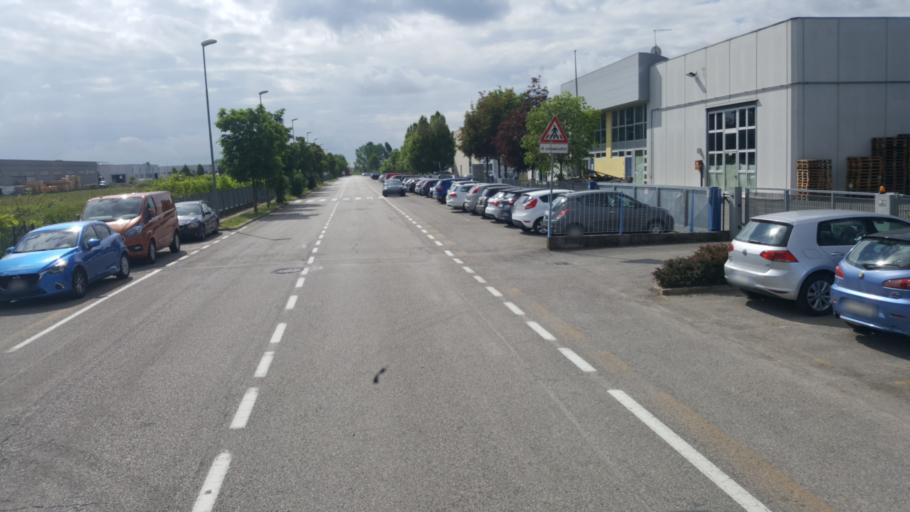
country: IT
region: Veneto
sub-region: Provincia di Venezia
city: Noventa di Piave
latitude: 45.6745
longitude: 12.5554
